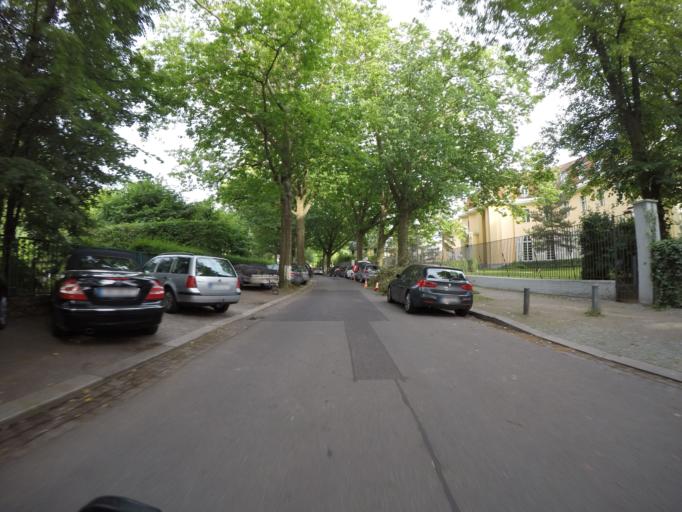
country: DE
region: Berlin
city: Grunewald
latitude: 52.4841
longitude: 13.2601
